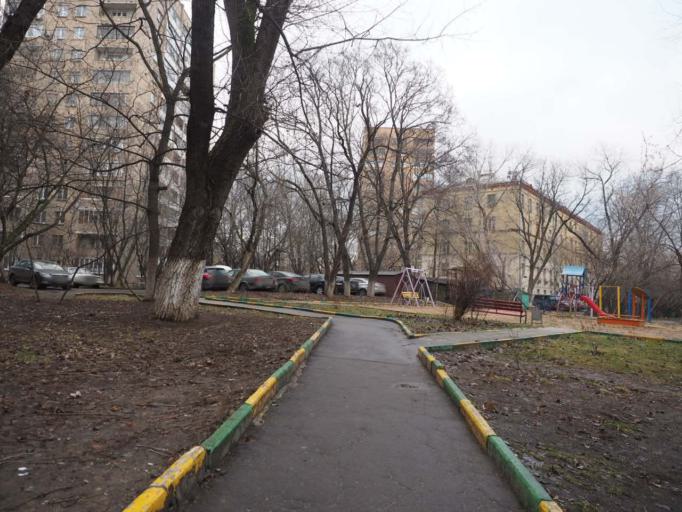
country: RU
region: Moskovskaya
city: Leninskiye Gory
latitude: 55.6950
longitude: 37.5713
